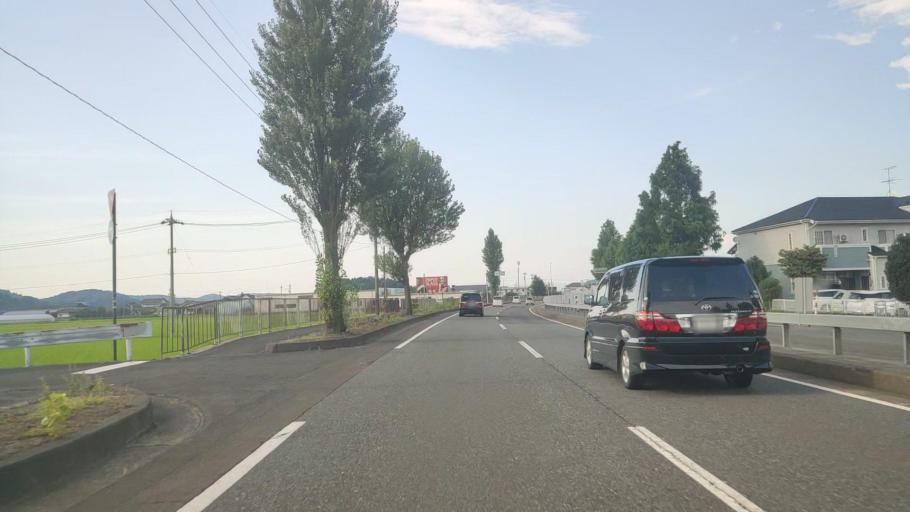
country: JP
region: Fukui
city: Sabae
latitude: 35.9880
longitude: 136.1989
